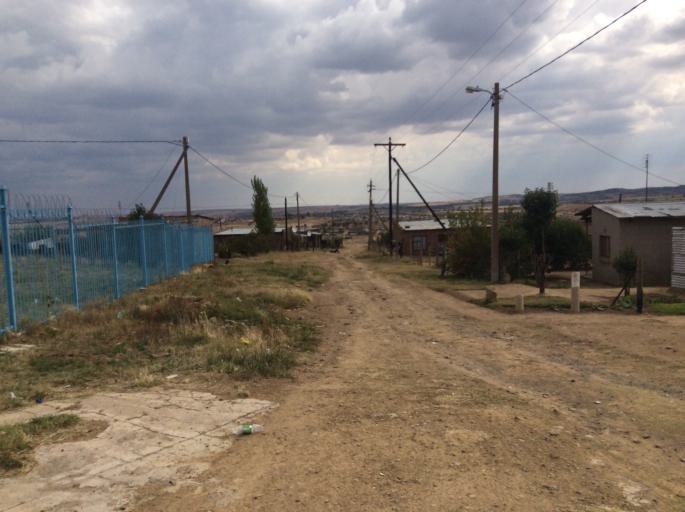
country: LS
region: Mafeteng
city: Mafeteng
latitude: -29.7230
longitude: 27.0312
